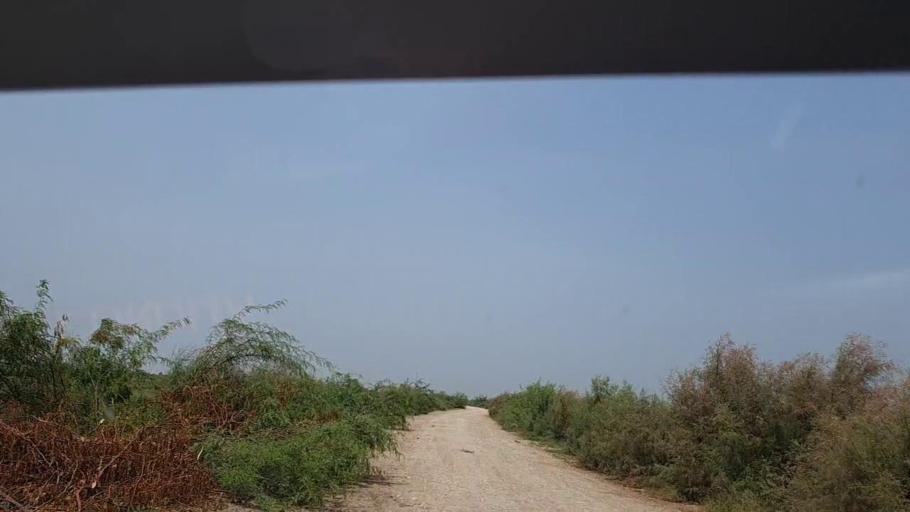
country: PK
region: Sindh
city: Adilpur
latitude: 27.9059
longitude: 69.2232
